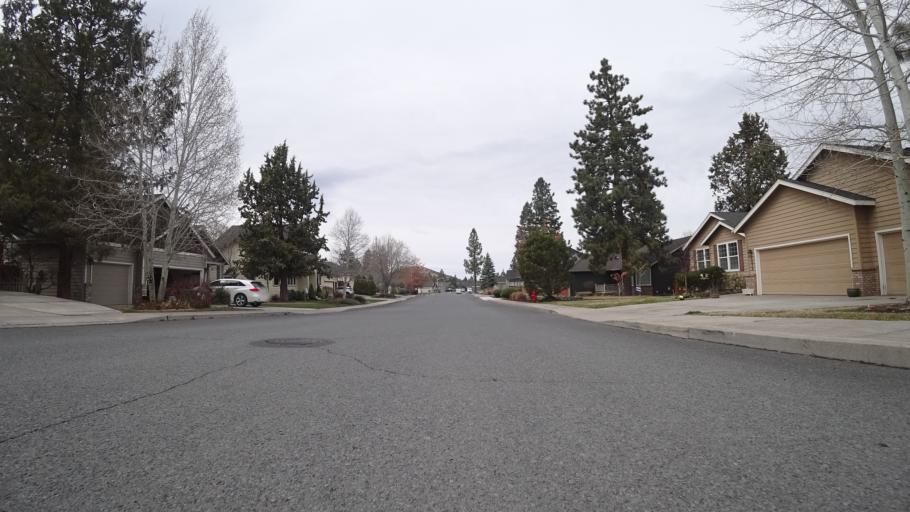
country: US
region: Oregon
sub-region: Deschutes County
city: Bend
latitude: 44.0398
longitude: -121.2751
